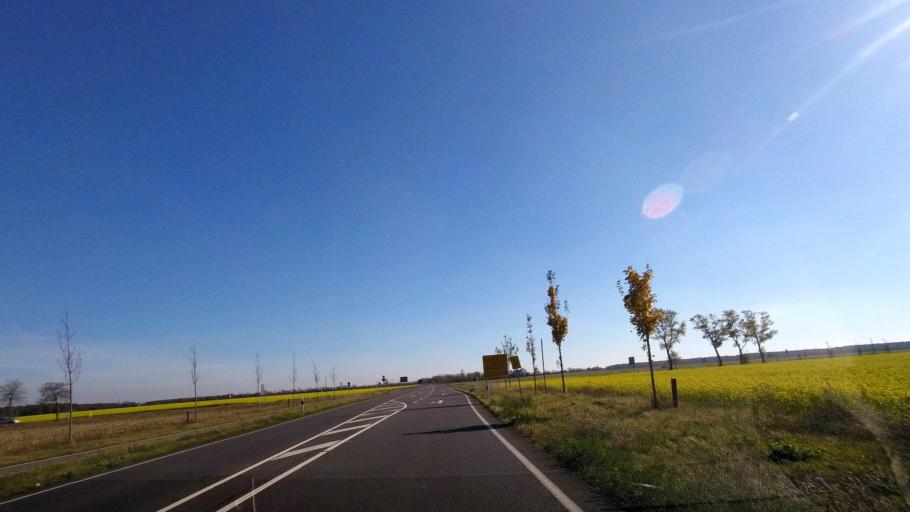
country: DE
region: Saxony-Anhalt
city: Muhlanger
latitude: 51.8468
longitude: 12.7667
